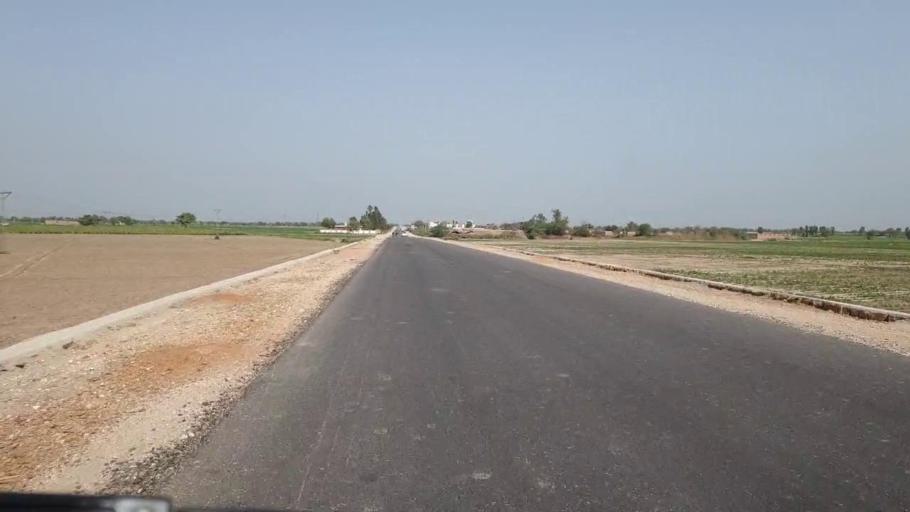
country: PK
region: Sindh
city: Sakrand
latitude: 26.2655
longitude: 68.1737
